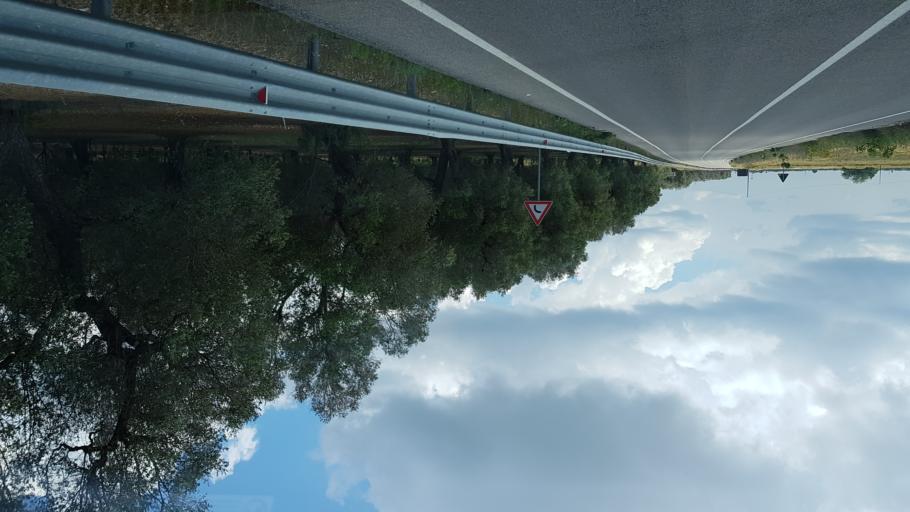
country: IT
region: Apulia
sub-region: Provincia di Brindisi
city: Mesagne
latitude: 40.5091
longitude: 17.8272
